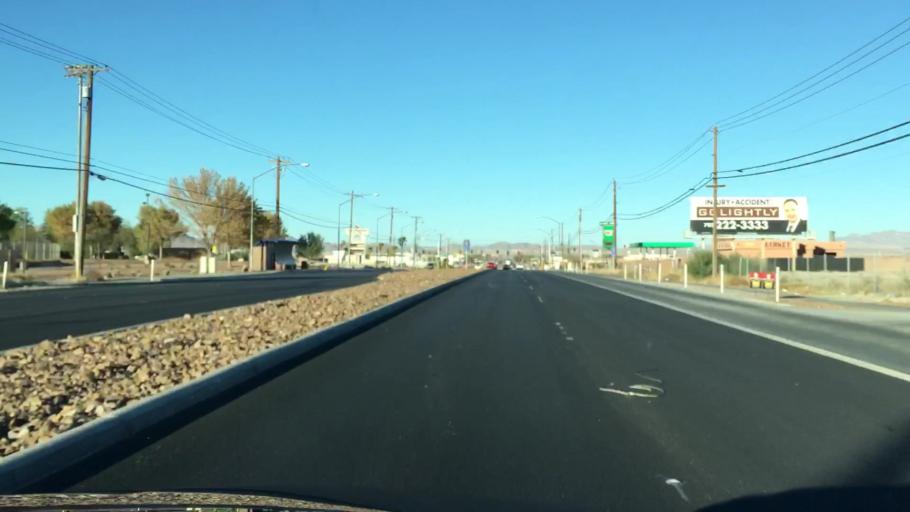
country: US
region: Nevada
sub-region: Clark County
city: Sunrise Manor
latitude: 36.2239
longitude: -115.0828
